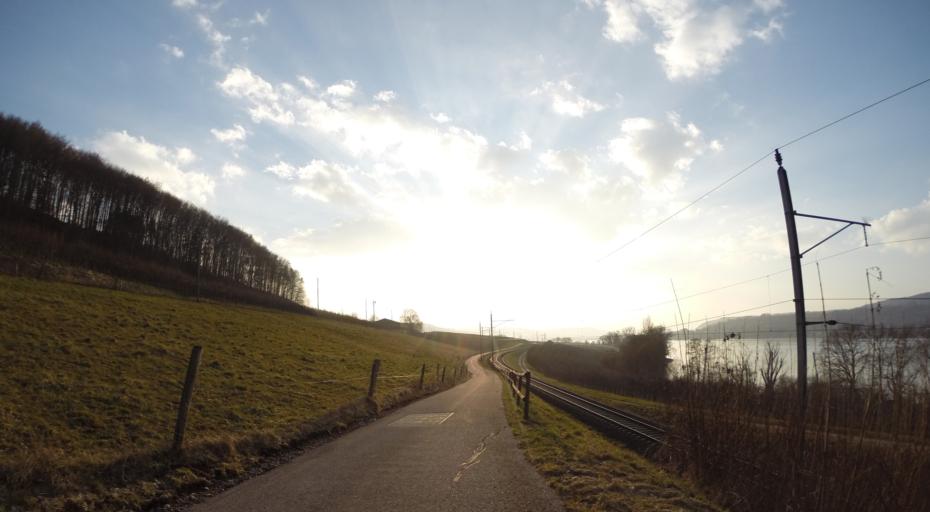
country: CH
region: Thurgau
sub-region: Frauenfeld District
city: Steckborn
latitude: 47.6514
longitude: 8.9399
